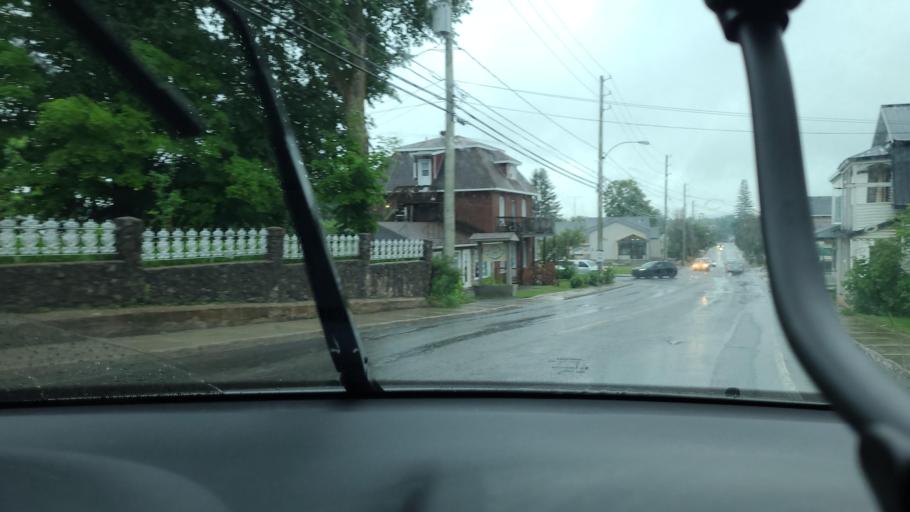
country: CA
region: Quebec
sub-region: Outaouais
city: Saint-Andre-Avellin
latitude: 45.7276
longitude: -75.0530
